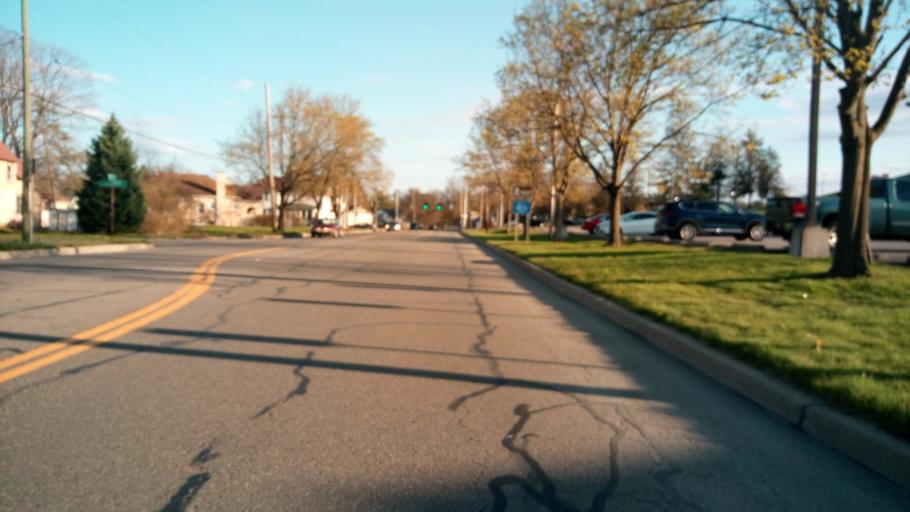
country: US
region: New York
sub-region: Chemung County
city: Elmira Heights
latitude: 42.1161
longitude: -76.8272
